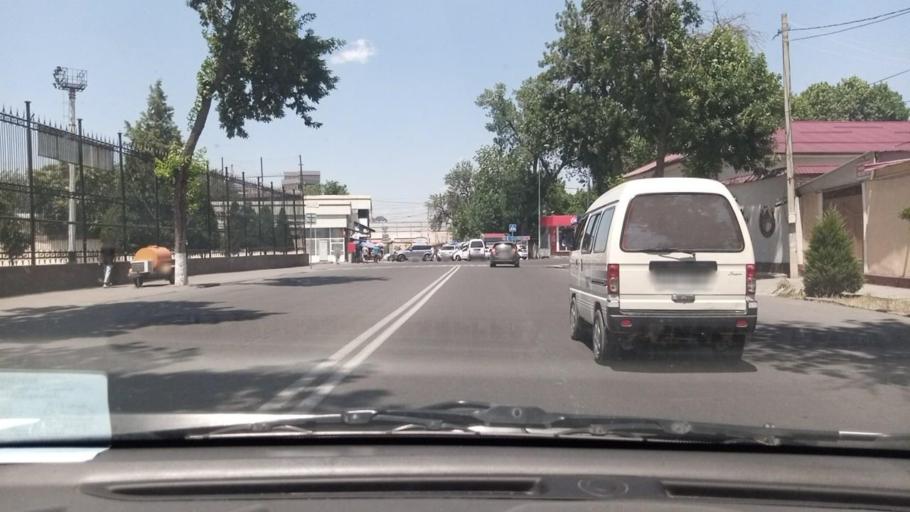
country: UZ
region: Toshkent Shahri
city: Tashkent
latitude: 41.2766
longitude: 69.2742
